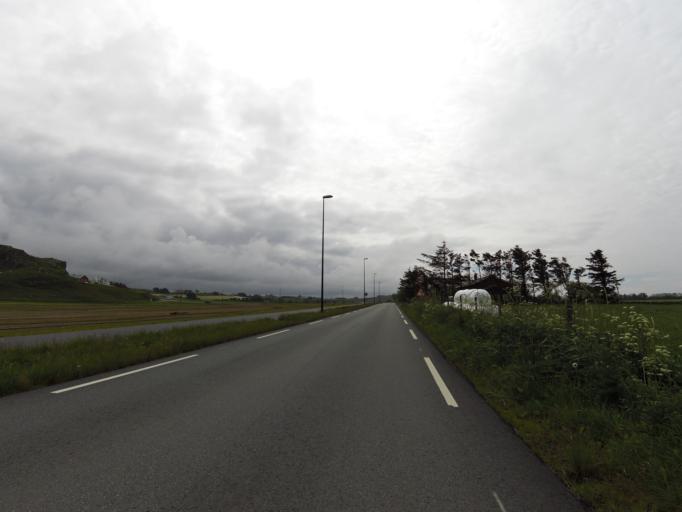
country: NO
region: Rogaland
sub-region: Klepp
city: Kleppe
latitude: 58.8413
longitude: 5.5693
